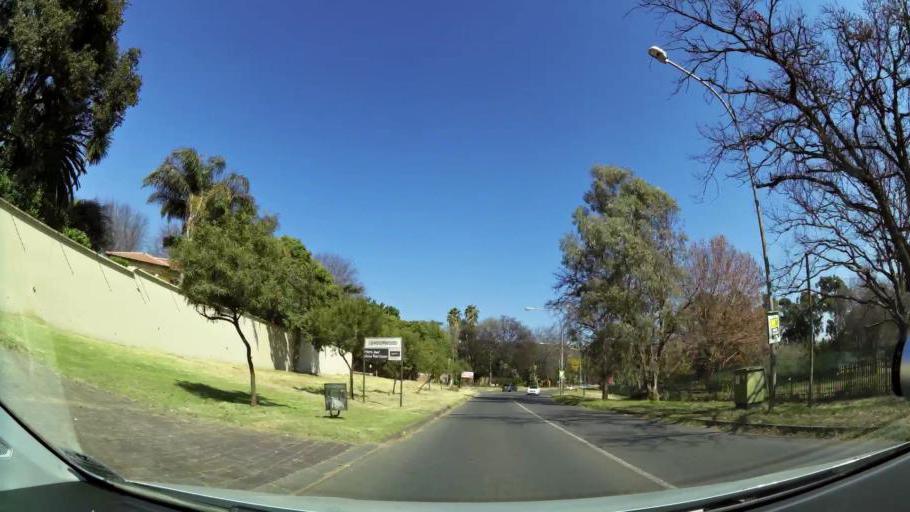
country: ZA
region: Gauteng
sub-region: City of Johannesburg Metropolitan Municipality
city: Modderfontein
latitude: -26.1594
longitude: 28.1178
